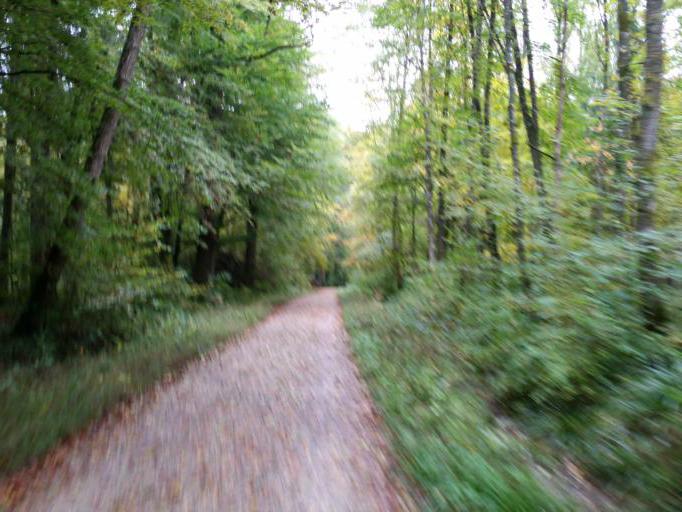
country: CH
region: Thurgau
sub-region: Arbon District
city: Uttwil
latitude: 47.5664
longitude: 9.3456
